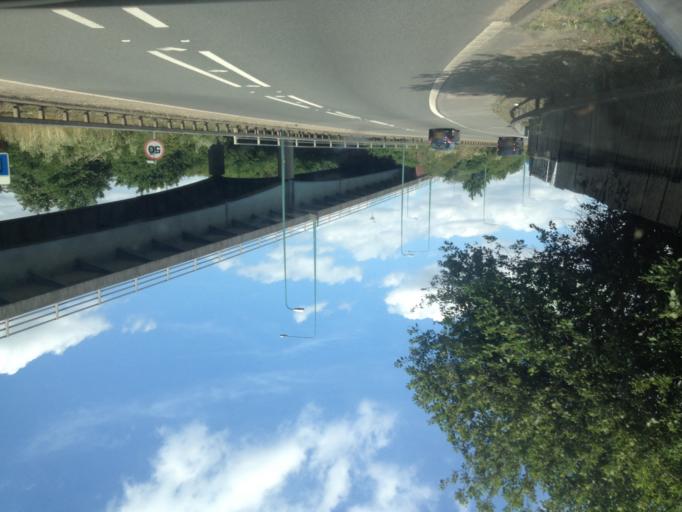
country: GB
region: England
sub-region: Greater London
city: Hendon
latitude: 51.5725
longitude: -0.2306
